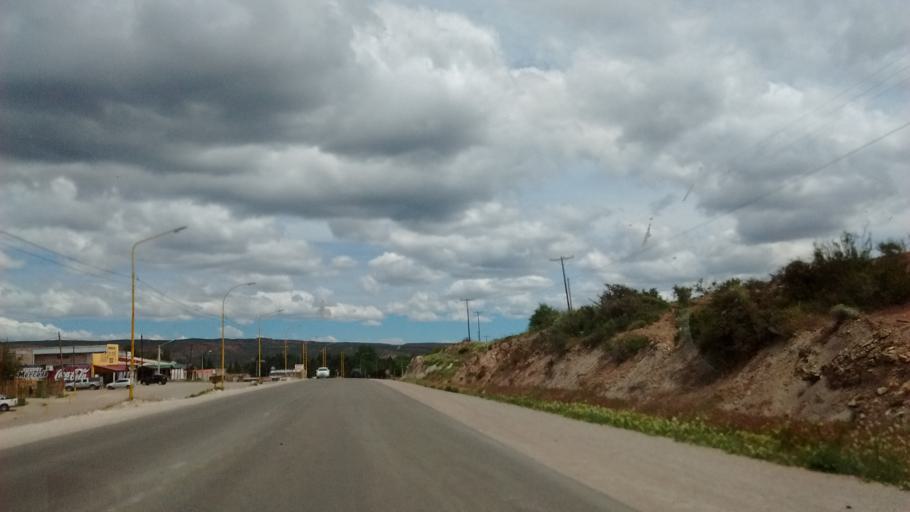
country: AR
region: Neuquen
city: Piedra del Aguila
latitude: -40.0449
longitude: -70.0728
